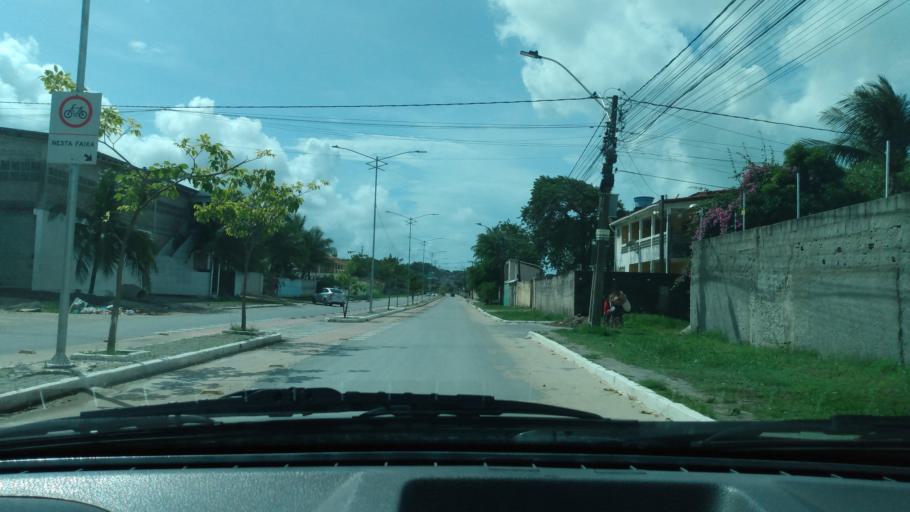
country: BR
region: Pernambuco
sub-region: Cabo De Santo Agostinho
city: Cabo
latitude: -8.3264
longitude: -34.9535
